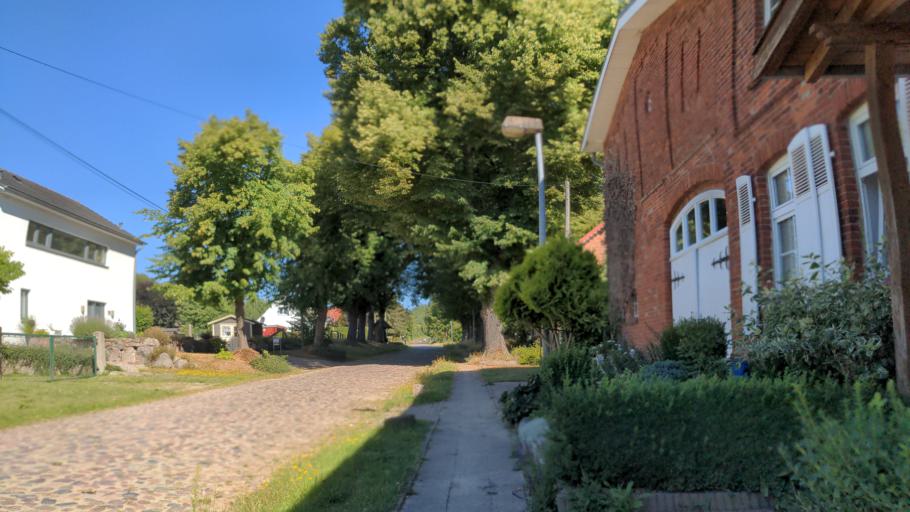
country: DE
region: Mecklenburg-Vorpommern
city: Selmsdorf
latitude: 53.8412
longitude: 10.8536
